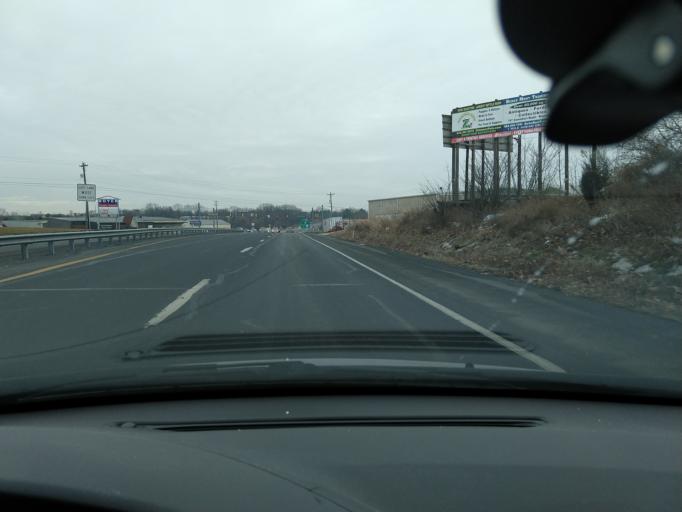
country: US
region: Pennsylvania
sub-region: Berks County
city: New Berlinville
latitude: 40.3360
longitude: -75.6214
